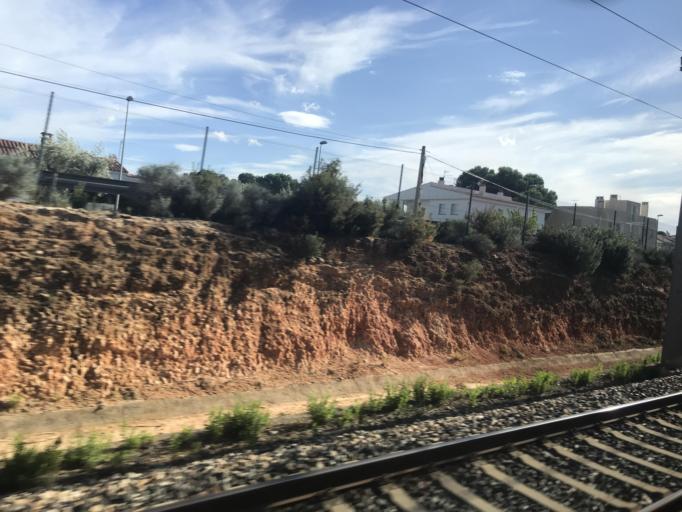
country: ES
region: Catalonia
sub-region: Provincia de Tarragona
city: L'Ampolla
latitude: 40.8255
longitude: 0.7307
